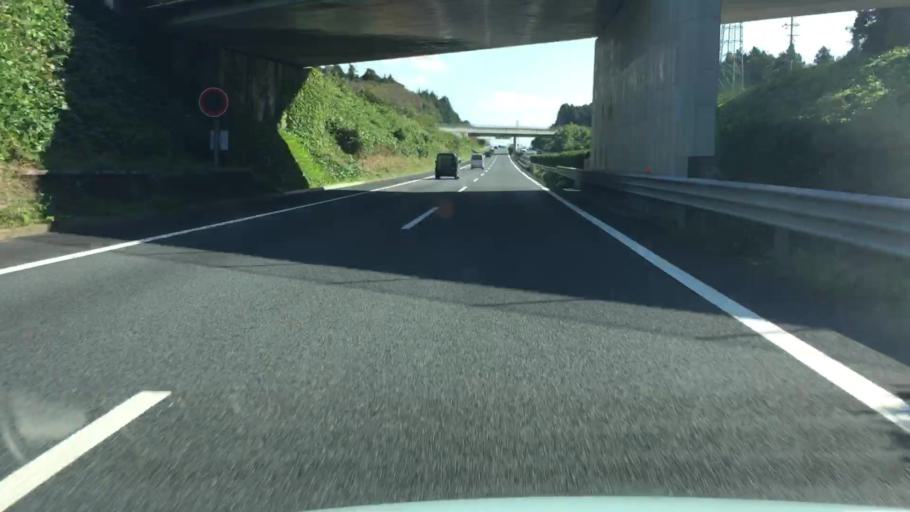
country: JP
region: Ibaraki
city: Tomobe
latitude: 36.3170
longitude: 140.3265
